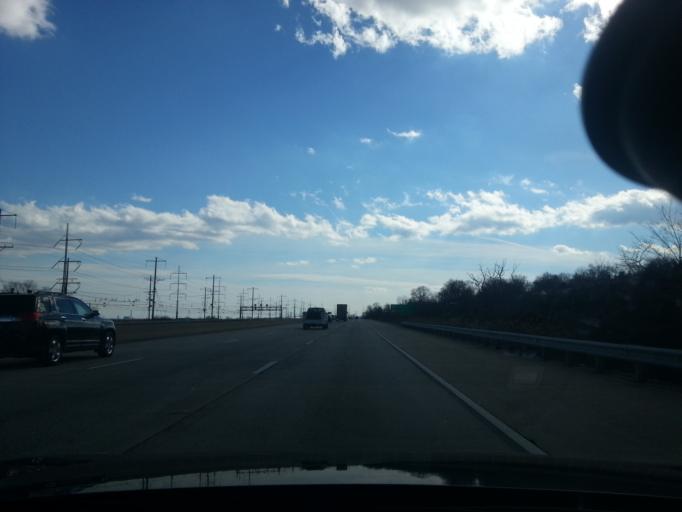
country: US
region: Delaware
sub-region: New Castle County
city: Edgemoor
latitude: 39.7675
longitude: -75.4855
